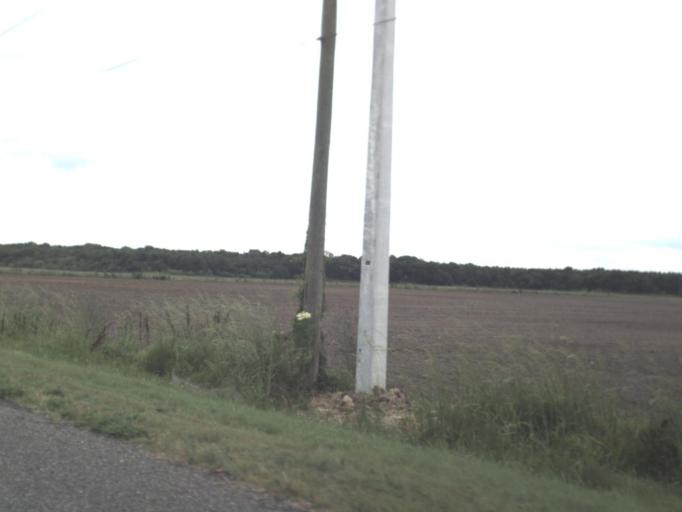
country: US
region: Florida
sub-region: Nassau County
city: Callahan
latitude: 30.6163
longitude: -81.8417
